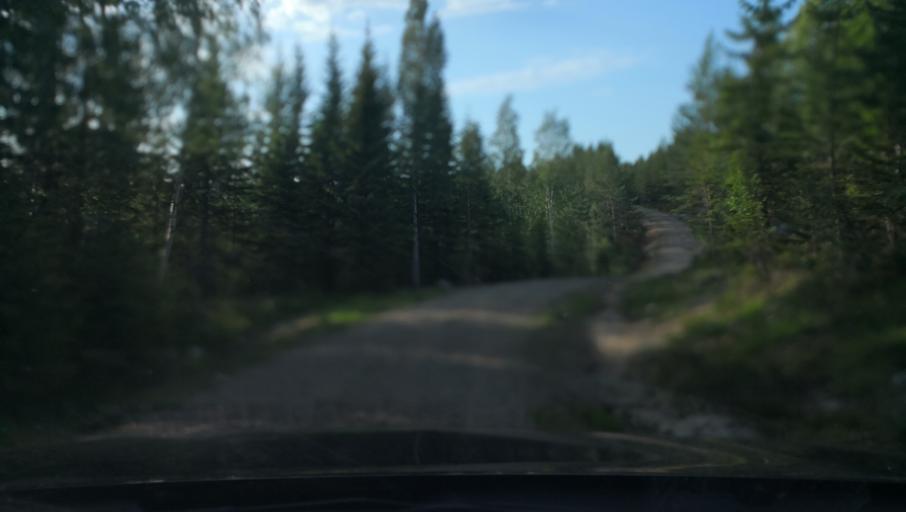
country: SE
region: Dalarna
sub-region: Smedjebackens Kommun
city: Smedjebacken
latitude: 60.0639
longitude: 15.3085
